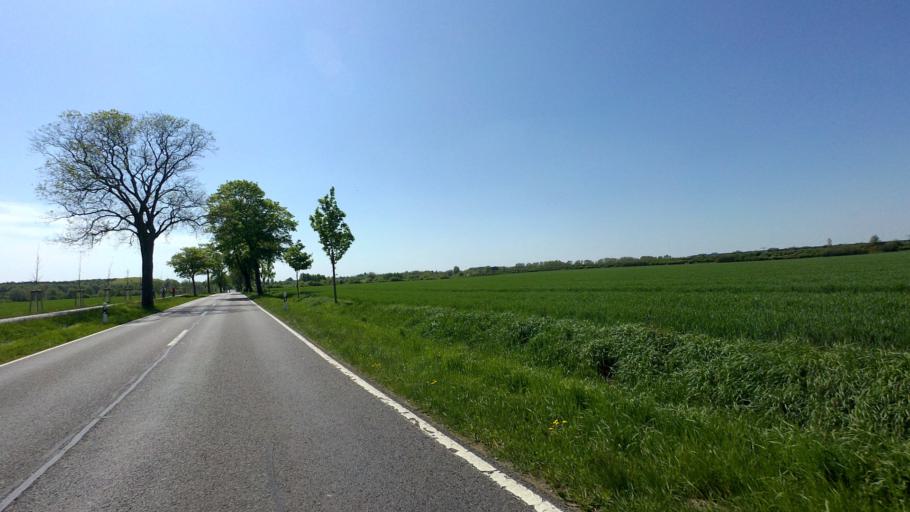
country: DE
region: Brandenburg
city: Schulzendorf
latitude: 52.3553
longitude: 13.5575
